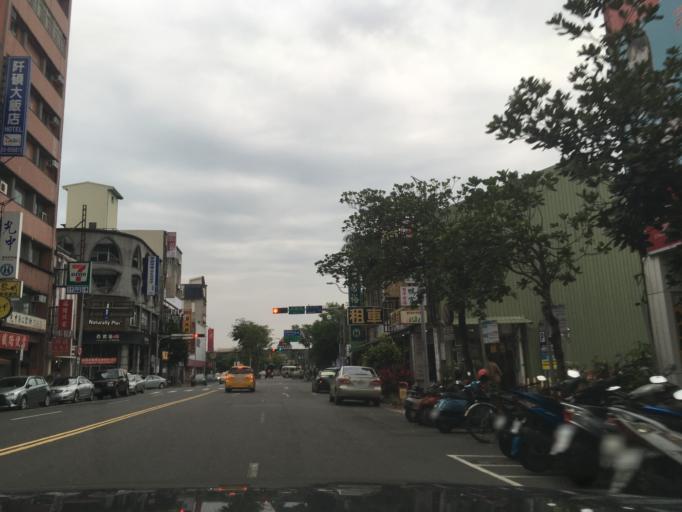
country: TW
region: Taiwan
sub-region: Yilan
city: Yilan
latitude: 24.7550
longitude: 121.7560
